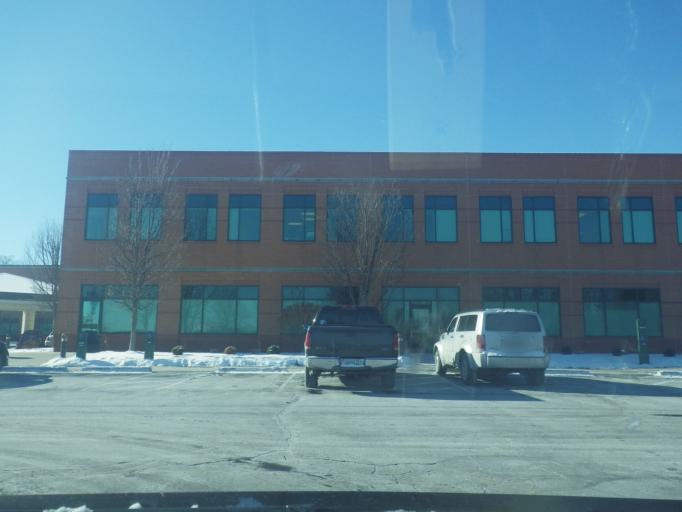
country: US
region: Indiana
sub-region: Marion County
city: Cumberland
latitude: 39.7764
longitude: -85.9932
